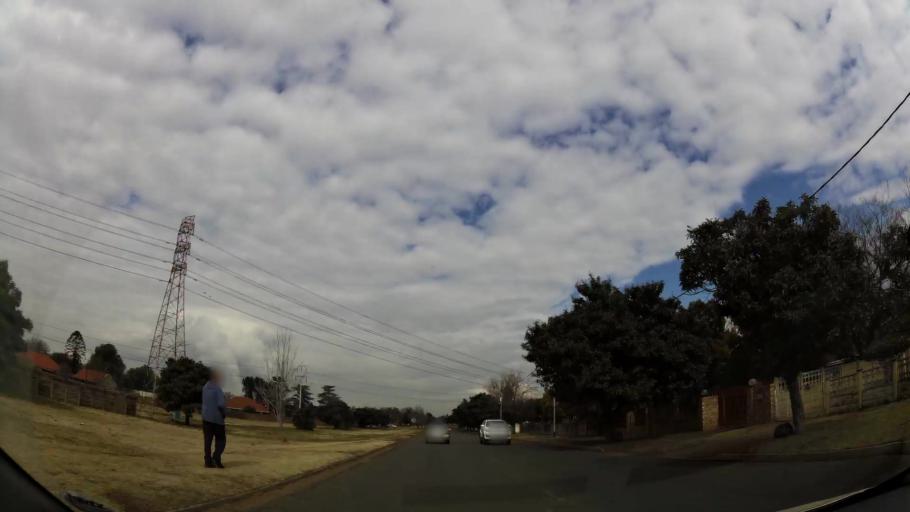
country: ZA
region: Gauteng
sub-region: Sedibeng District Municipality
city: Vereeniging
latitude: -26.6494
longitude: 27.9691
